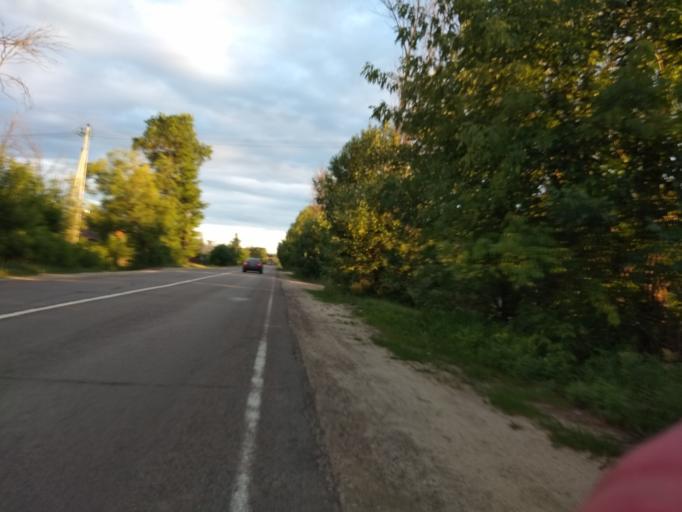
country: RU
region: Moskovskaya
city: Kerva
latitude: 55.5953
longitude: 39.7024
